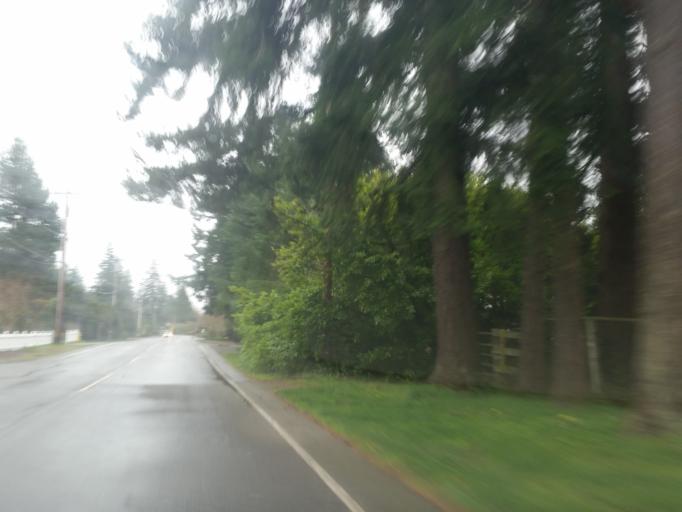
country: US
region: Washington
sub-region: Snohomish County
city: Edmonds
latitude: 47.8130
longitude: -122.3548
